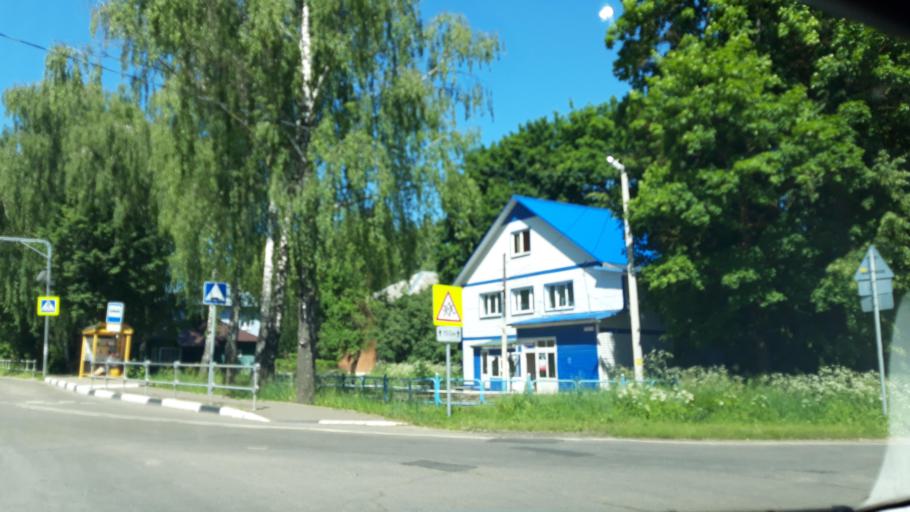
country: RU
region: Moskovskaya
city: Solnechnogorsk
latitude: 56.1678
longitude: 36.9572
